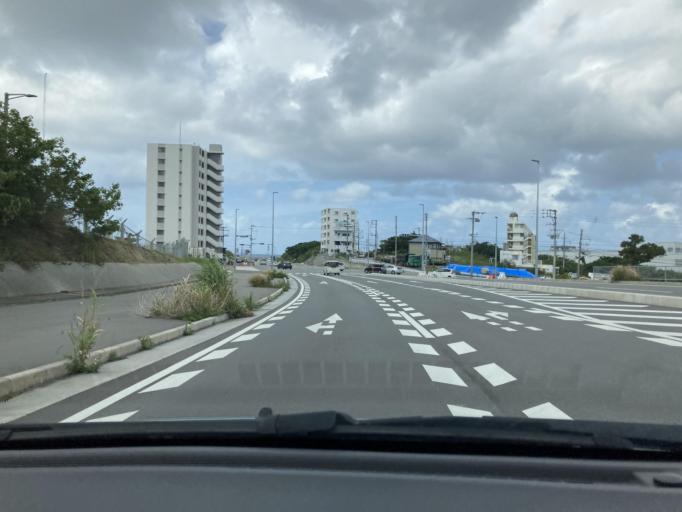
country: JP
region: Okinawa
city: Ginowan
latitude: 26.2684
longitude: 127.7097
